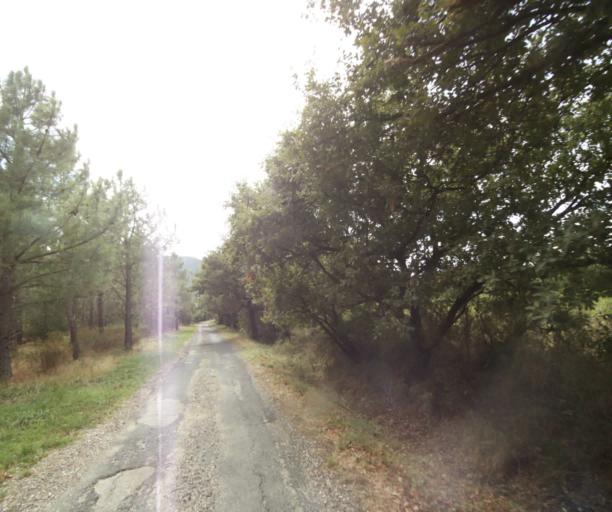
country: FR
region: Languedoc-Roussillon
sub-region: Departement des Pyrenees-Orientales
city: Argelers
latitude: 42.5367
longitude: 3.0169
